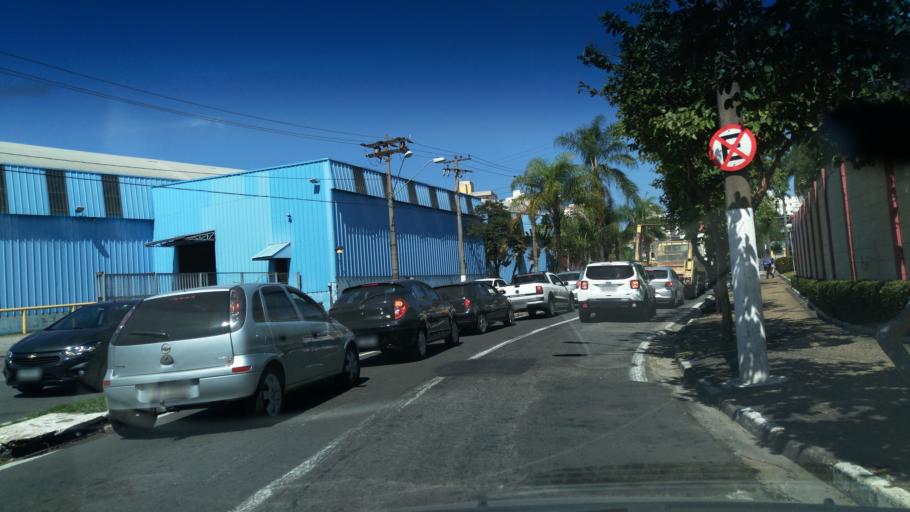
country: BR
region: Sao Paulo
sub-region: Valinhos
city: Valinhos
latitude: -22.9713
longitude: -46.9932
